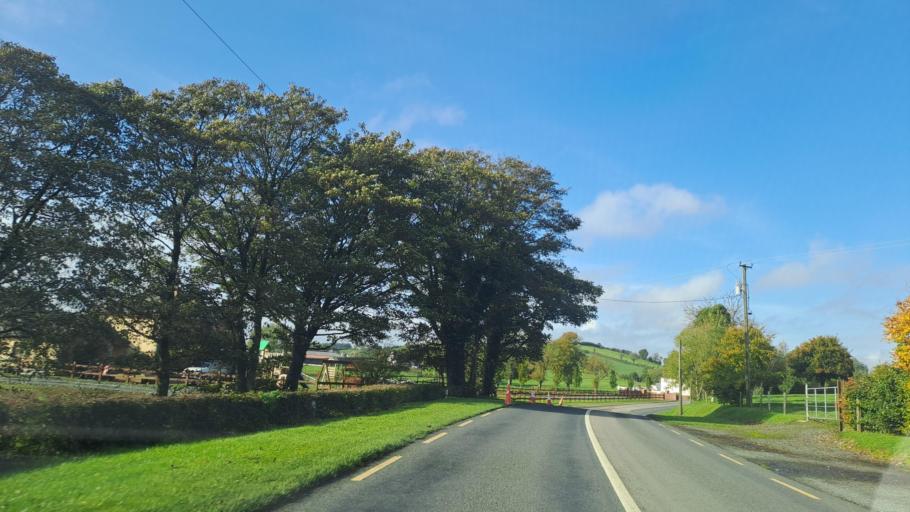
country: IE
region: Ulster
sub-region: An Cabhan
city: Cootehill
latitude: 54.0621
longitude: -7.0433
